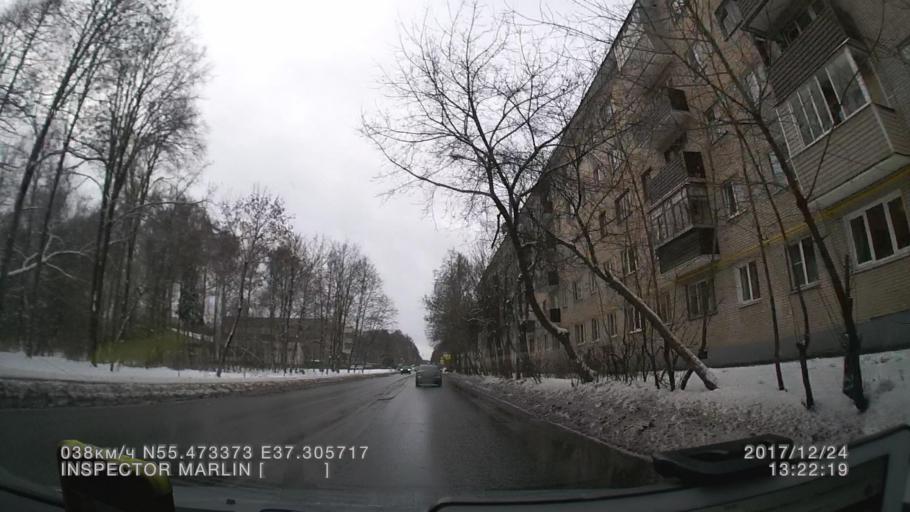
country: RU
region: Moskovskaya
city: Troitsk
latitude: 55.4733
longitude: 37.3055
